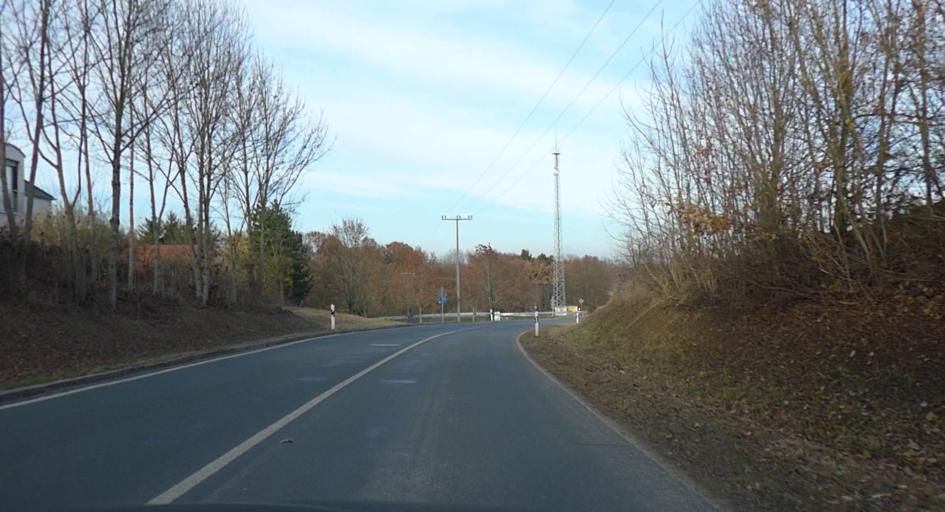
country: DE
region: Bavaria
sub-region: Regierungsbezirk Mittelfranken
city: Bubenreuth
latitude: 49.6175
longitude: 11.0288
